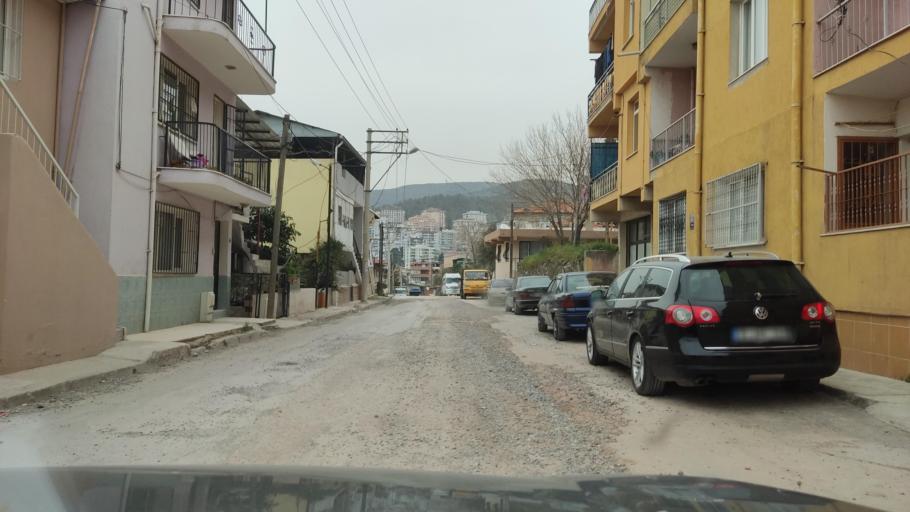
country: TR
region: Izmir
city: Karsiyaka
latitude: 38.4970
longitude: 27.0699
